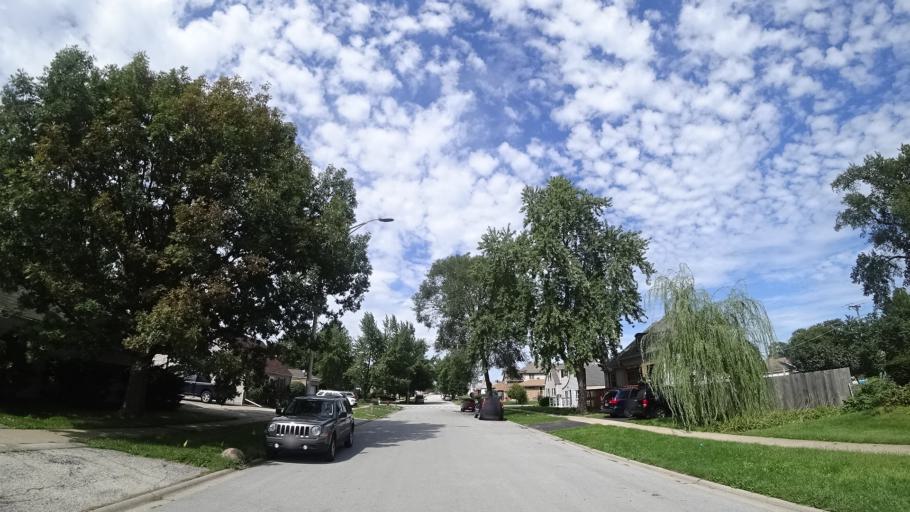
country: US
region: Illinois
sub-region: Cook County
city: Chicago Ridge
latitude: 41.7172
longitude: -87.7774
